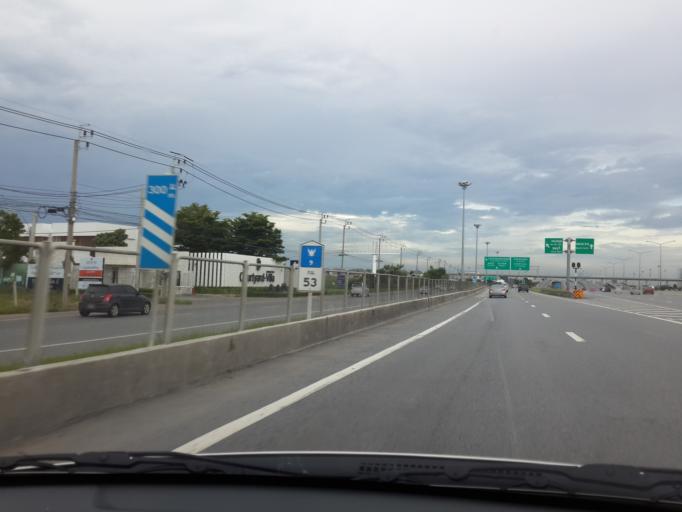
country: TH
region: Bangkok
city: Saphan Sung
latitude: 13.7417
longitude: 100.7029
